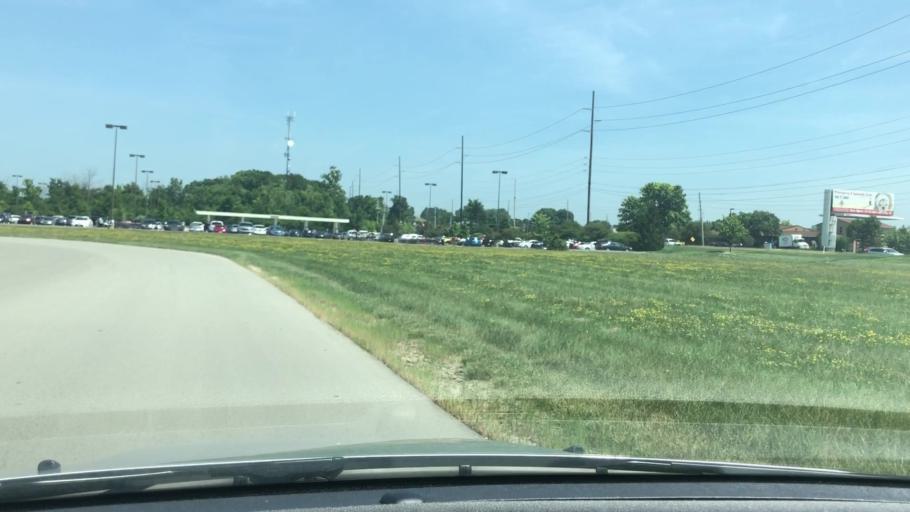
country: US
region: Indiana
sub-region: Hamilton County
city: Fishers
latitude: 39.9132
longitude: -86.0642
